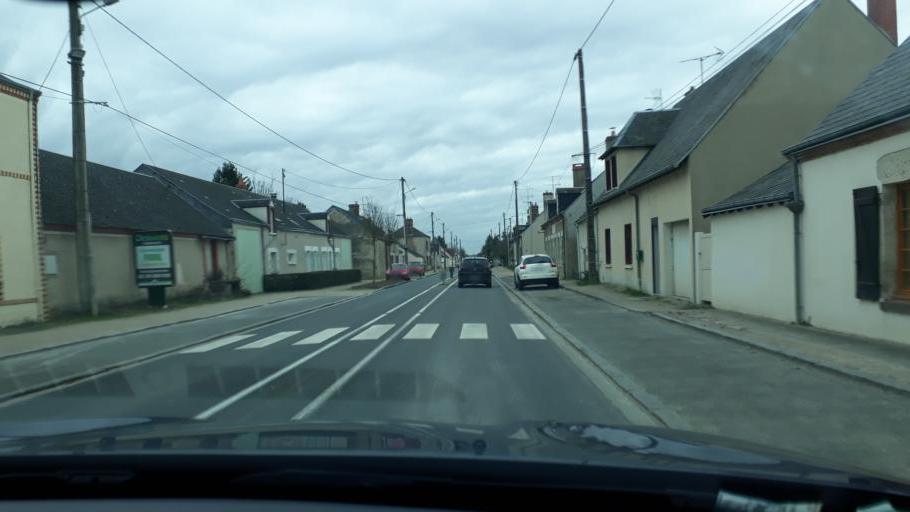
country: FR
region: Centre
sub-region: Departement du Loiret
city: Ascheres-le-Marche
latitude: 48.0405
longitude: 1.9822
